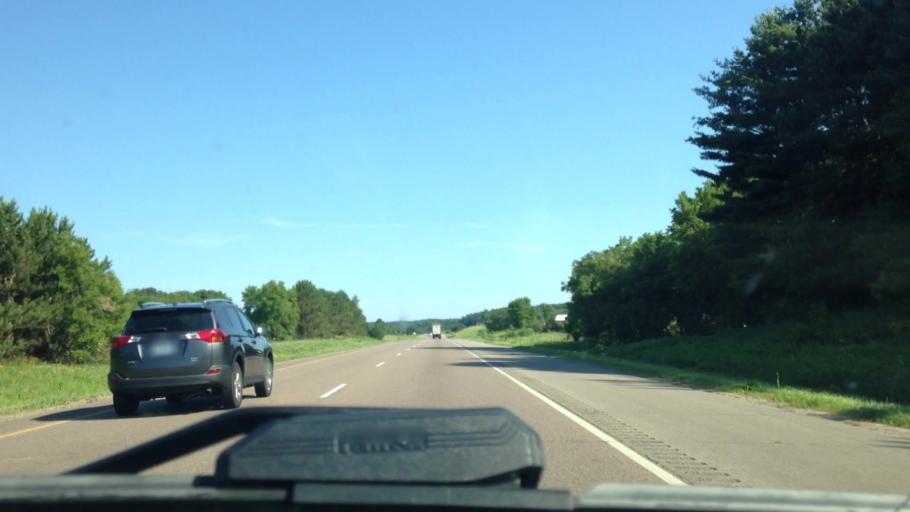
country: US
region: Wisconsin
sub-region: Eau Claire County
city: Fall Creek
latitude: 44.7031
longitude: -91.3423
